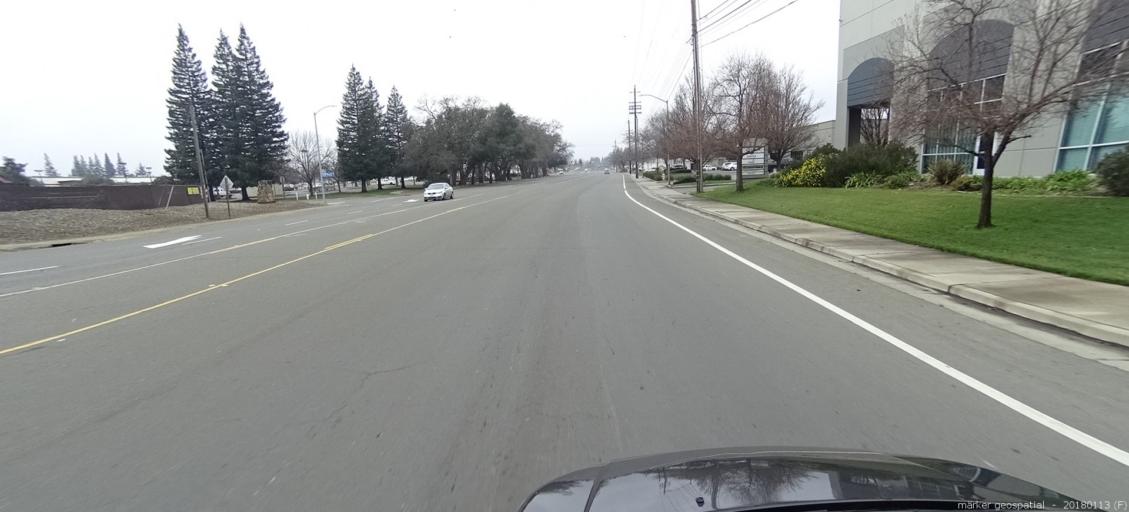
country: US
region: California
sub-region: Sacramento County
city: Gold River
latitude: 38.5901
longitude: -121.2614
